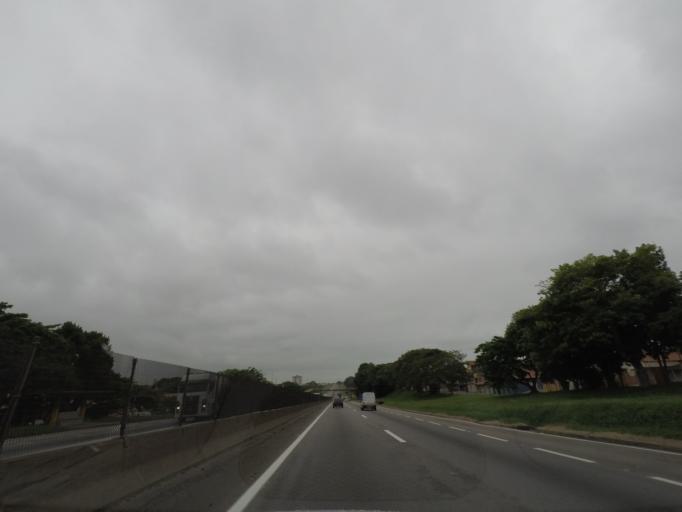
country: BR
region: Sao Paulo
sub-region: Taubate
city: Taubate
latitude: -23.0309
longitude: -45.5483
